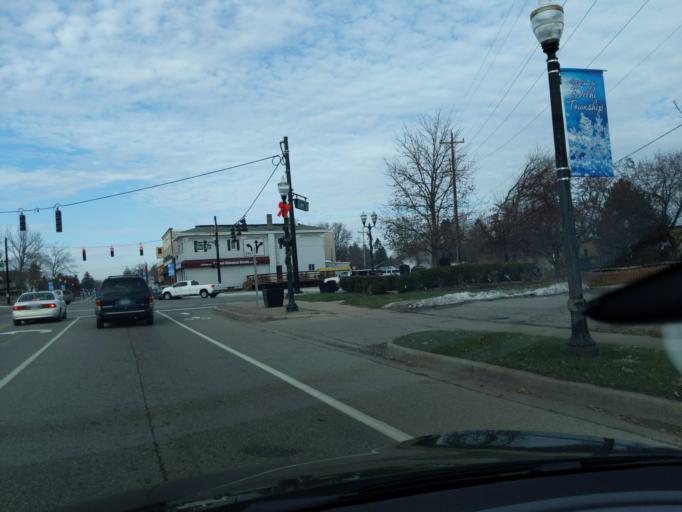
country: US
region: Michigan
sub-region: Ingham County
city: Holt
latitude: 42.6399
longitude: -84.5148
